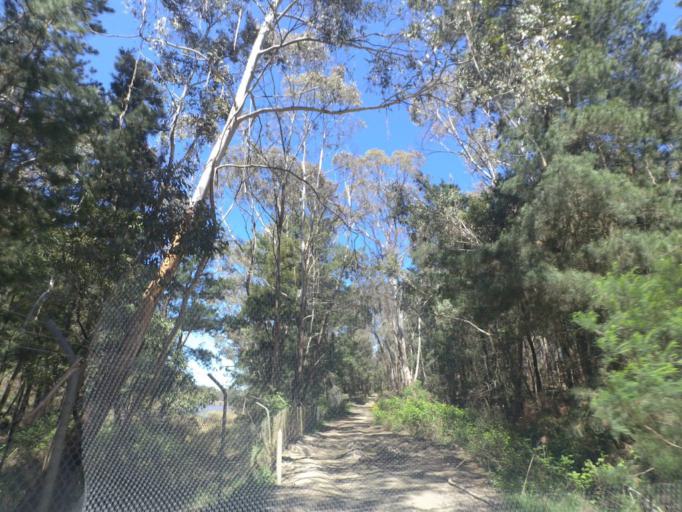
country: AU
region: Victoria
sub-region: Hume
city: Sunbury
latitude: -37.3904
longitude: 144.5532
